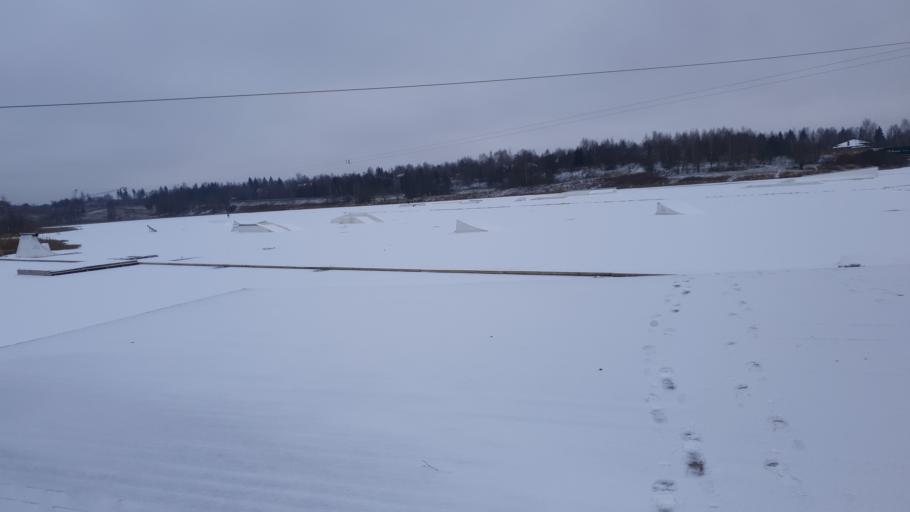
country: LT
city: Skaidiskes
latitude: 54.6380
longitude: 25.3761
